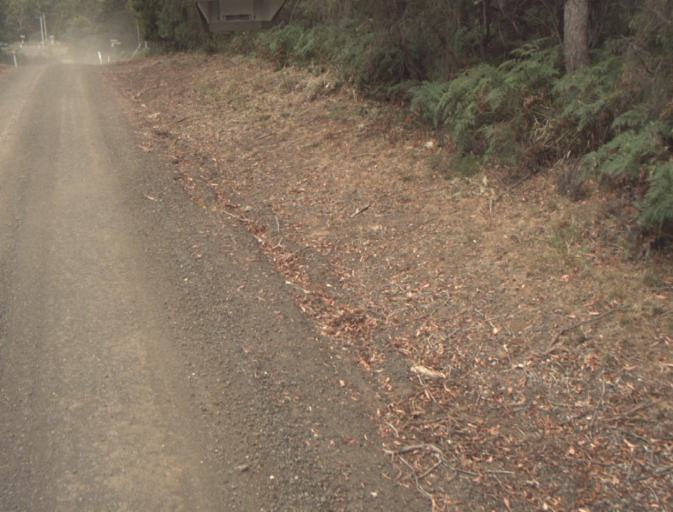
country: AU
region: Tasmania
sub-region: Launceston
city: Mayfield
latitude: -41.2766
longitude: 147.0475
